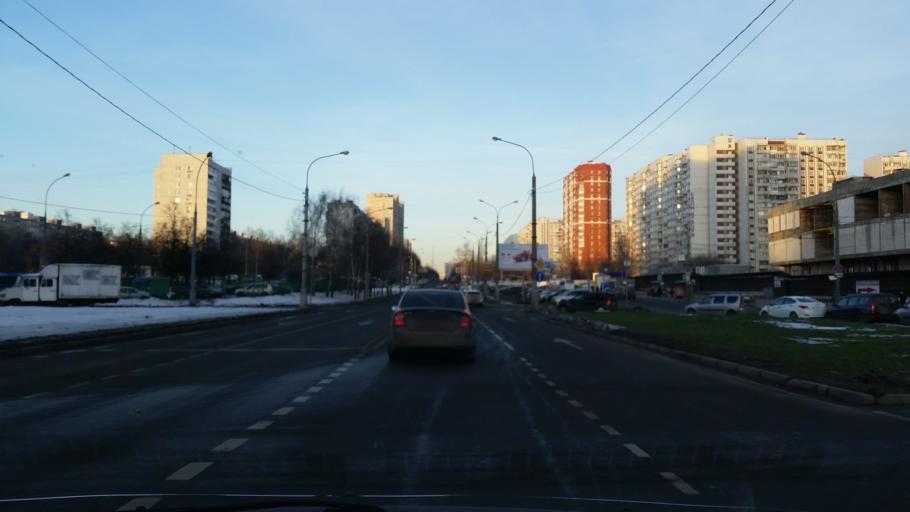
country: RU
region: Moscow
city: Nagornyy
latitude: 55.6212
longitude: 37.6082
